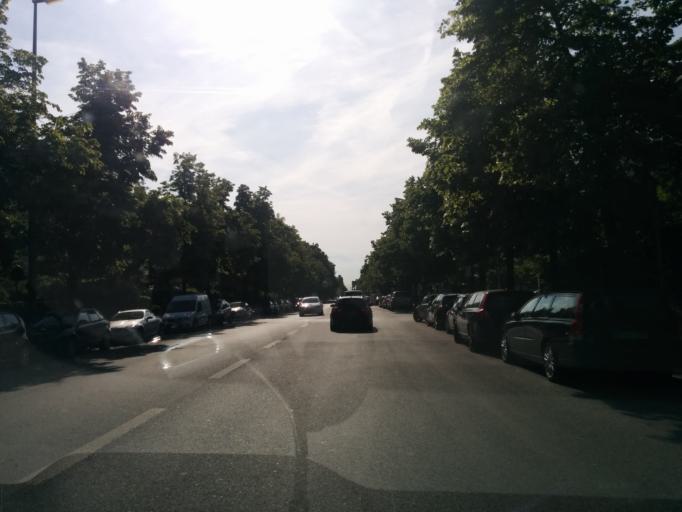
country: DE
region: Bavaria
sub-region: Upper Bavaria
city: Munich
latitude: 48.1506
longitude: 11.5426
